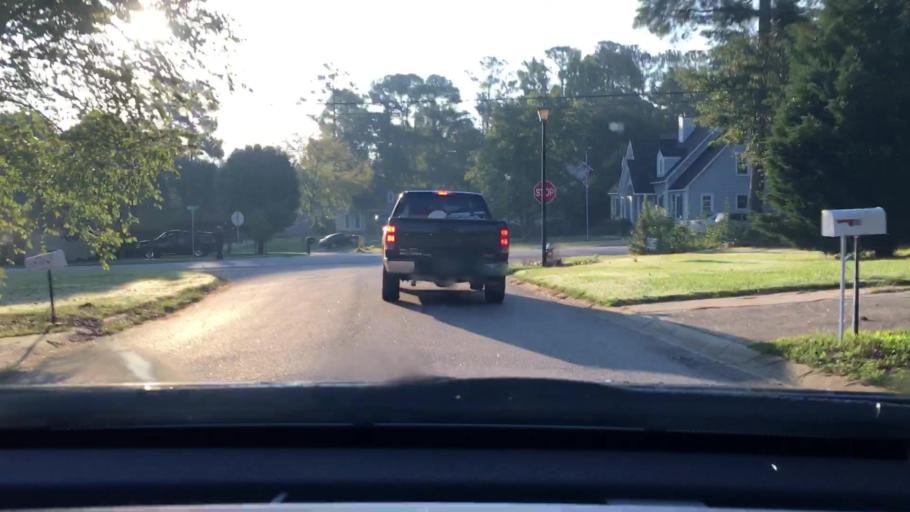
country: US
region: South Carolina
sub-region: Lexington County
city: Irmo
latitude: 34.1002
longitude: -81.1538
